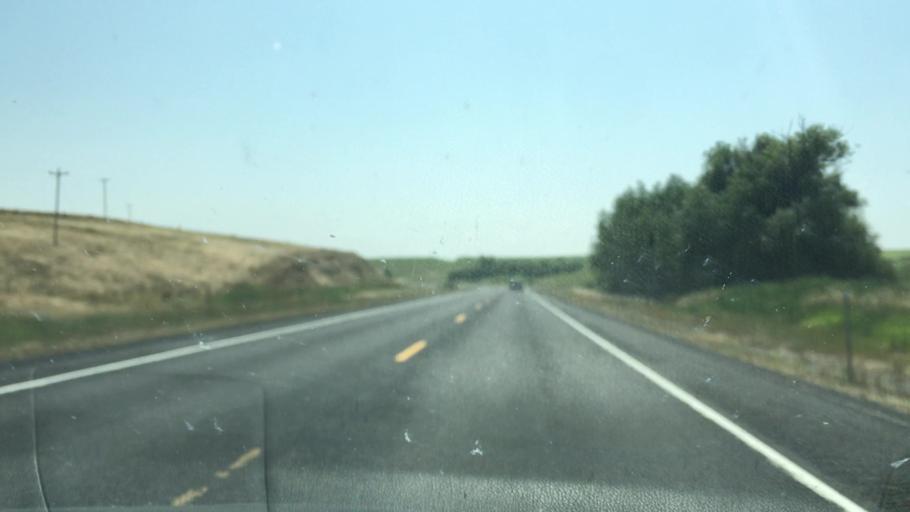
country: US
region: Idaho
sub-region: Lewis County
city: Nezperce
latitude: 46.2233
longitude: -116.4379
